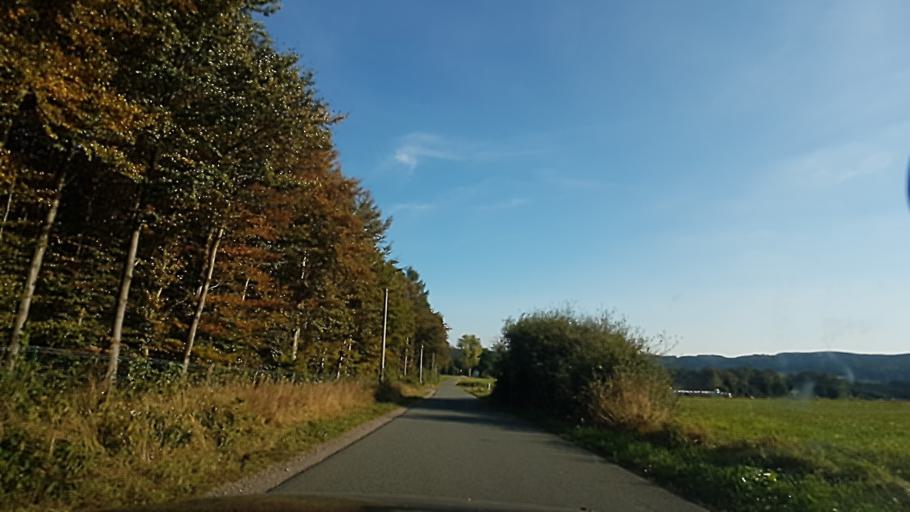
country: DE
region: North Rhine-Westphalia
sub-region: Regierungsbezirk Koln
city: Marienheide
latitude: 51.1249
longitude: 7.4852
